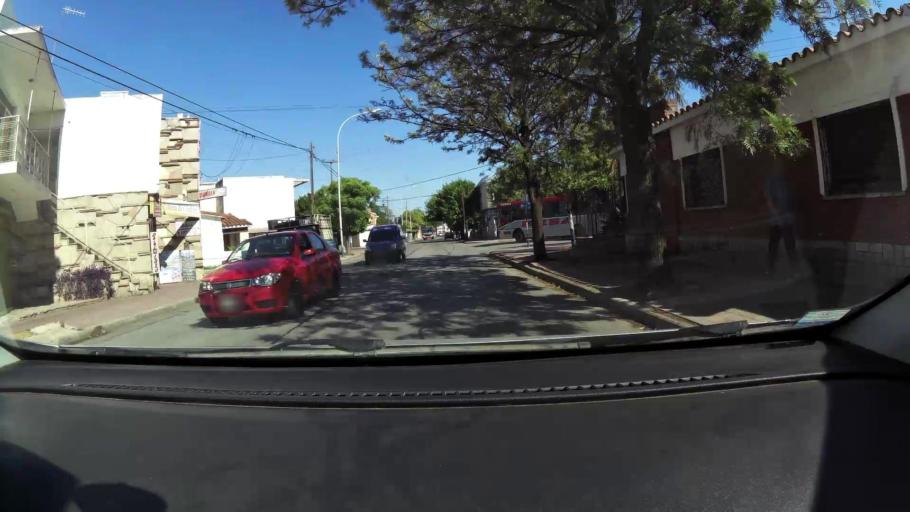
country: AR
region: Cordoba
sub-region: Departamento de Capital
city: Cordoba
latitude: -31.4355
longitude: -64.1677
